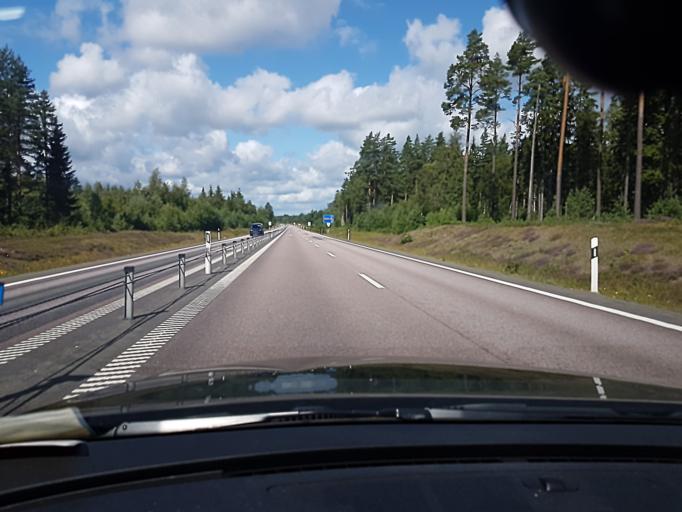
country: SE
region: Kalmar
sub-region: Emmaboda Kommun
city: Emmaboda
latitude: 56.7337
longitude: 15.5335
